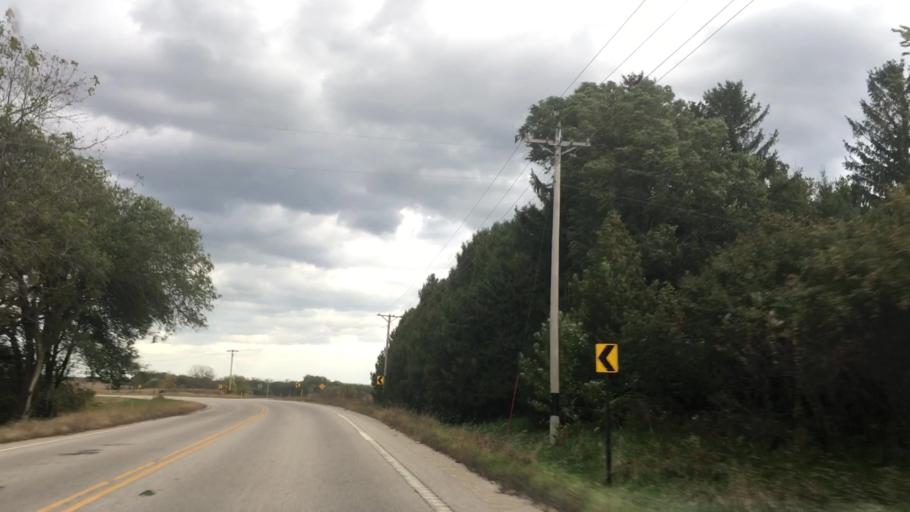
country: US
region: Minnesota
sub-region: Fillmore County
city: Preston
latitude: 43.7315
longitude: -92.0363
